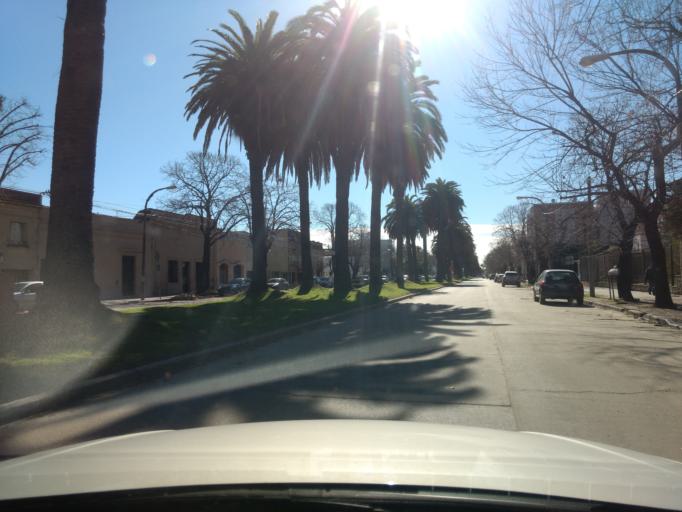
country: AR
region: Buenos Aires
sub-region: Partido de Lujan
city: Lujan
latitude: -34.5714
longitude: -59.1130
